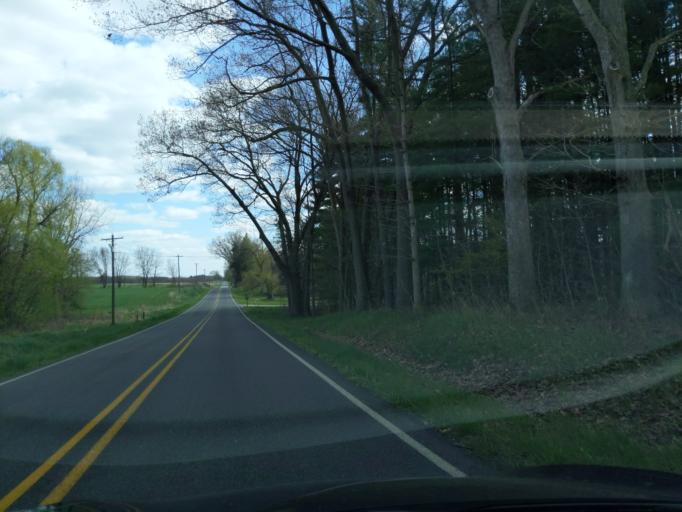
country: US
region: Michigan
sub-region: Ingham County
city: Leslie
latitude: 42.4135
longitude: -84.5416
